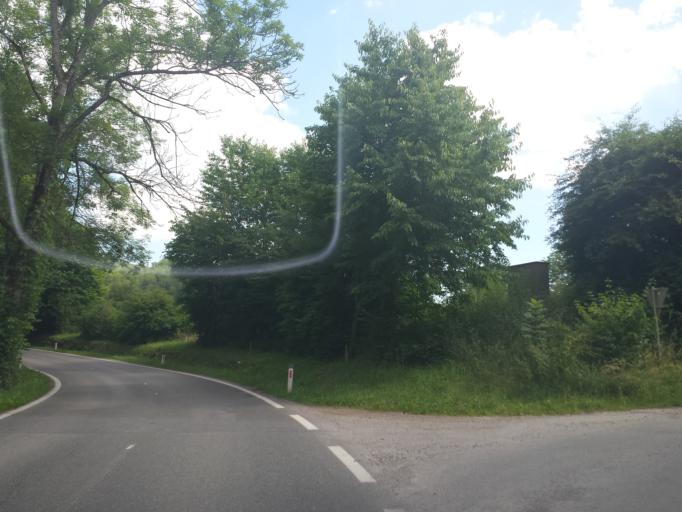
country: AT
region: Styria
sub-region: Politischer Bezirk Graz-Umgebung
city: Thal
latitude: 47.0696
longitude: 15.3633
